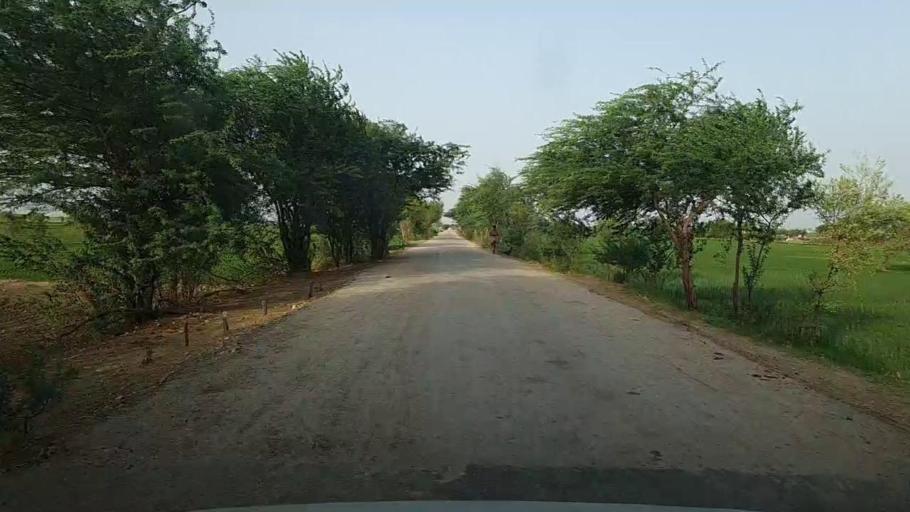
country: PK
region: Sindh
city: Mehar
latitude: 27.1609
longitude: 67.7613
